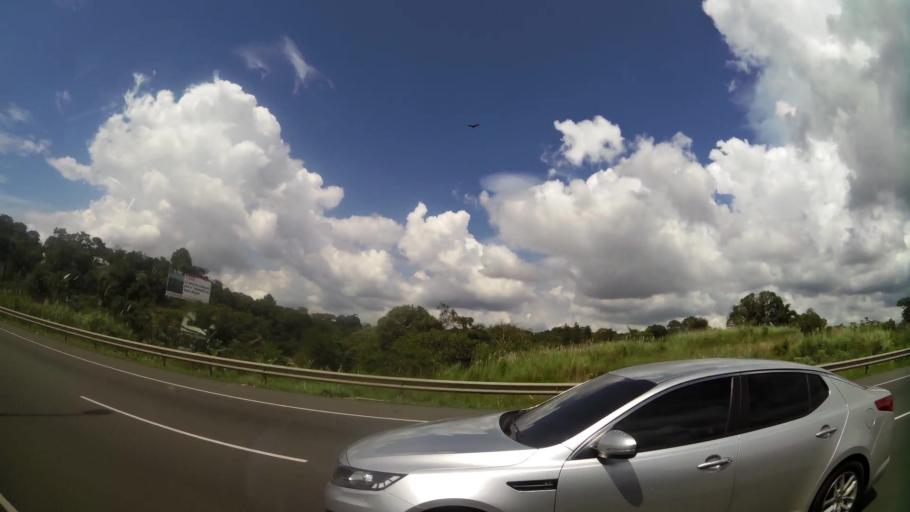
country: PA
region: Panama
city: Vista Alegre
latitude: 8.9412
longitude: -79.6763
